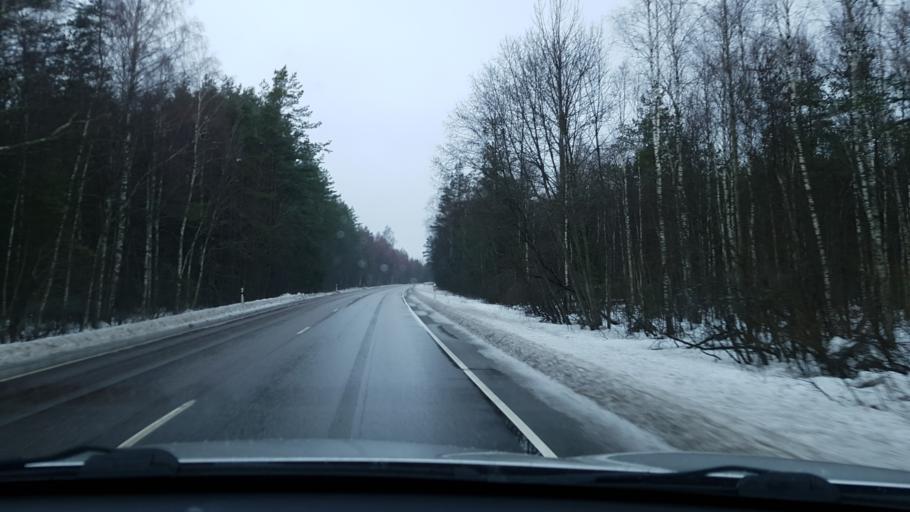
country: EE
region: Raplamaa
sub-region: Kehtna vald
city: Kehtna
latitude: 58.8652
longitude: 24.9905
